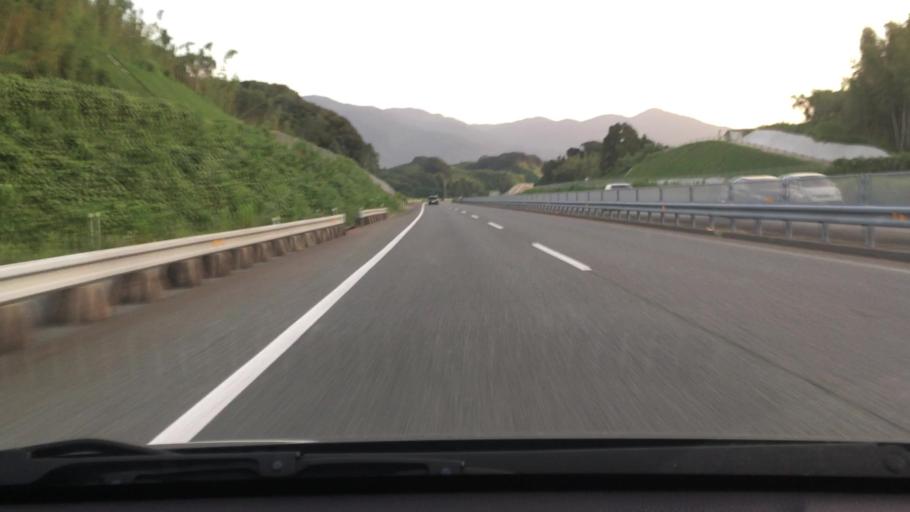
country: JP
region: Fukuoka
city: Maebaru-chuo
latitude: 33.5383
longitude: 130.1969
